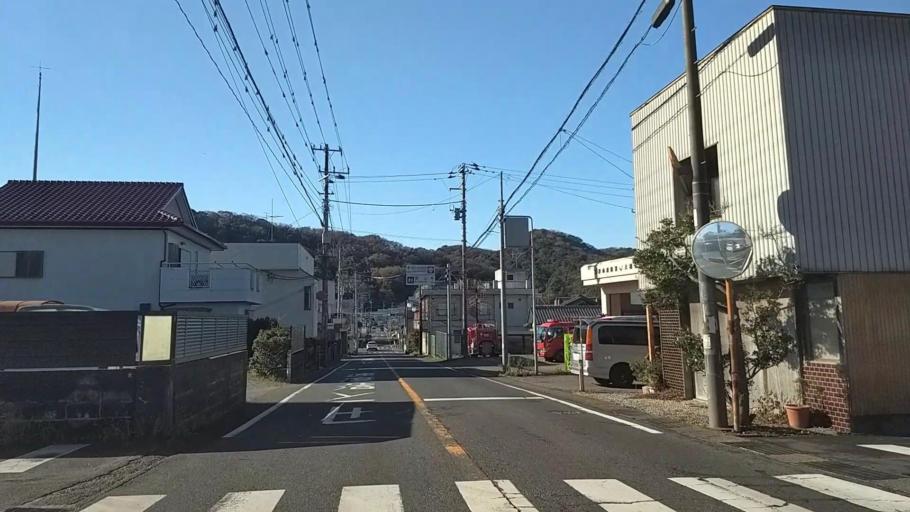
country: JP
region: Chiba
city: Futtsu
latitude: 35.2169
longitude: 139.8712
